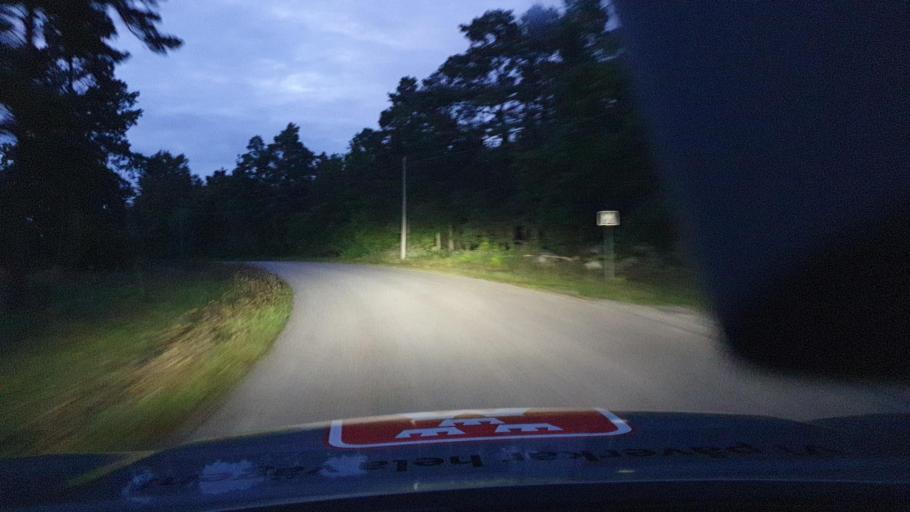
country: SE
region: Gotland
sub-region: Gotland
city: Slite
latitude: 57.7646
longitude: 18.6462
